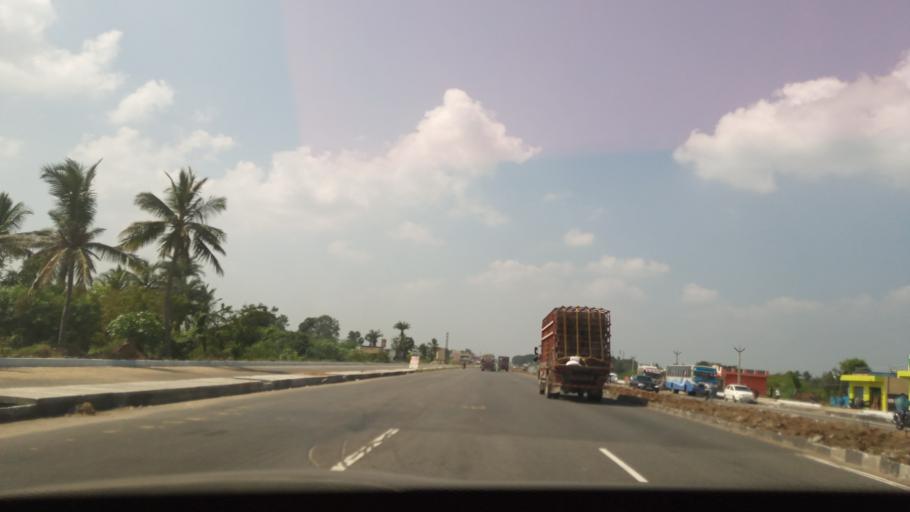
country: IN
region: Tamil Nadu
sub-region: Vellore
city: Walajapet
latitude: 12.9014
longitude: 79.4711
